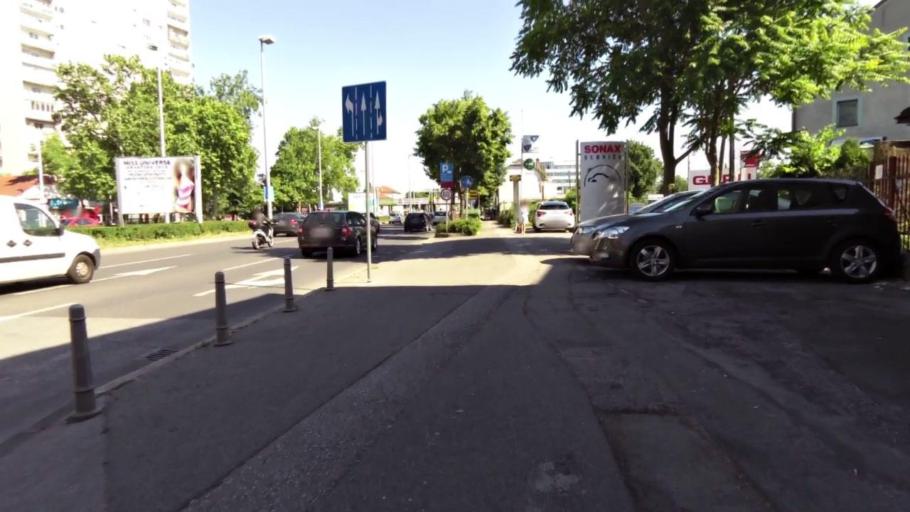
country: HR
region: Grad Zagreb
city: Zagreb
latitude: 45.8101
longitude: 16.0020
